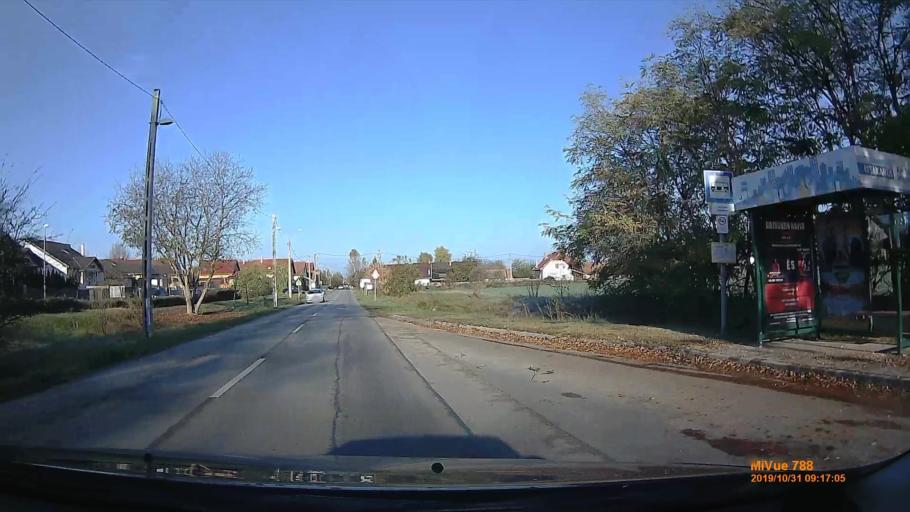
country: HU
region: Pest
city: Peteri
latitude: 47.4064
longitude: 19.4090
